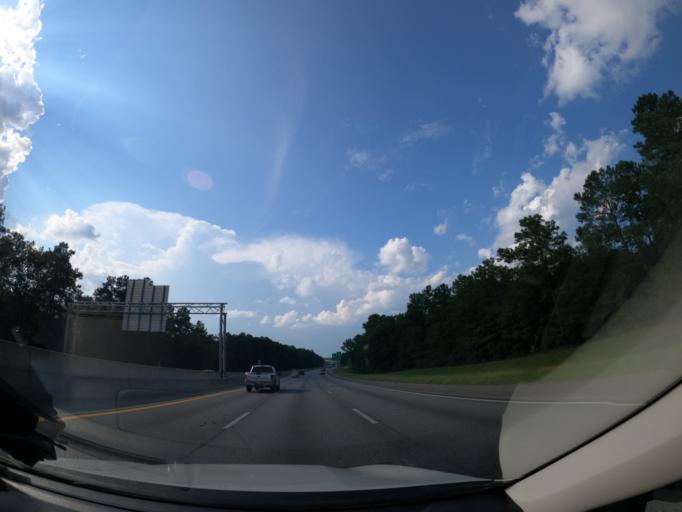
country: US
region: Georgia
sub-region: Columbia County
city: Martinez
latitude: 33.4379
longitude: -82.0718
